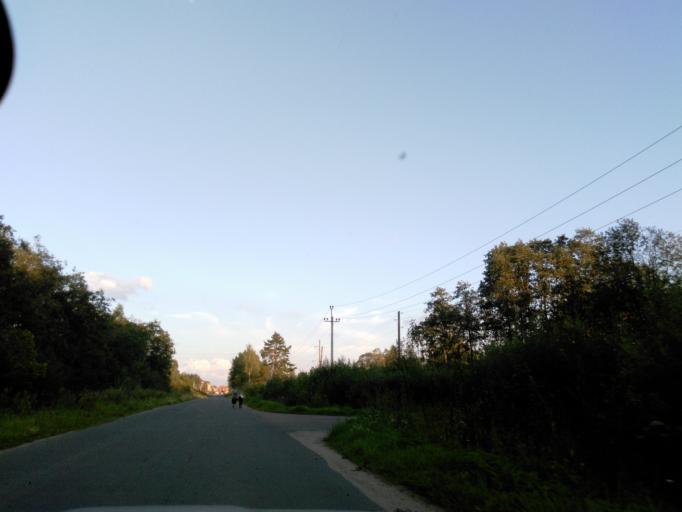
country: RU
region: Tverskaya
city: Konakovo
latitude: 56.6825
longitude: 36.7030
